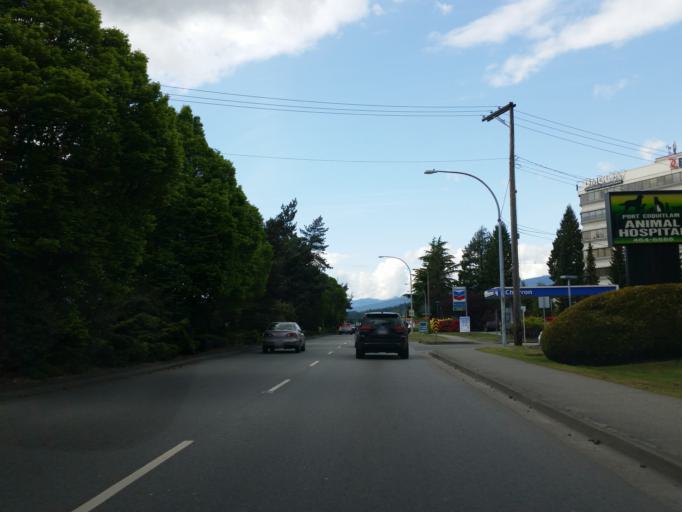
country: CA
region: British Columbia
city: Coquitlam
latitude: 49.2721
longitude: -122.7871
